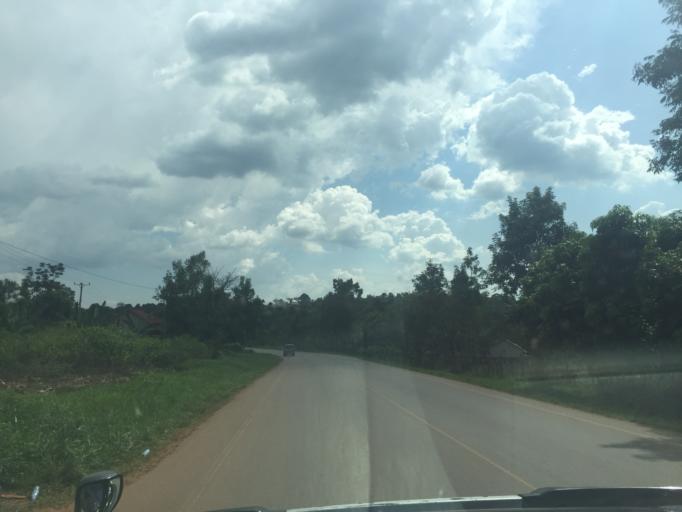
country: UG
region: Central Region
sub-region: Luwero District
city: Wobulenzi
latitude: 0.7008
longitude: 32.5234
